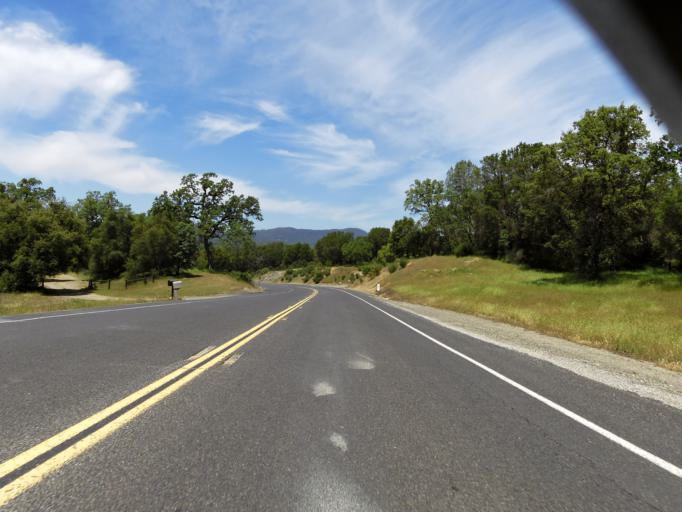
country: US
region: California
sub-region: Mariposa County
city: Mariposa
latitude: 37.4572
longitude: -119.8690
